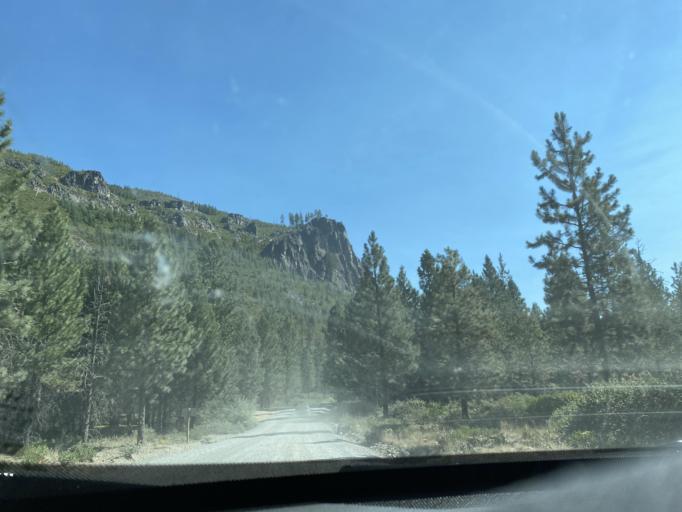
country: US
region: Oregon
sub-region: Deschutes County
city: Sunriver
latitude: 44.0321
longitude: -121.5551
